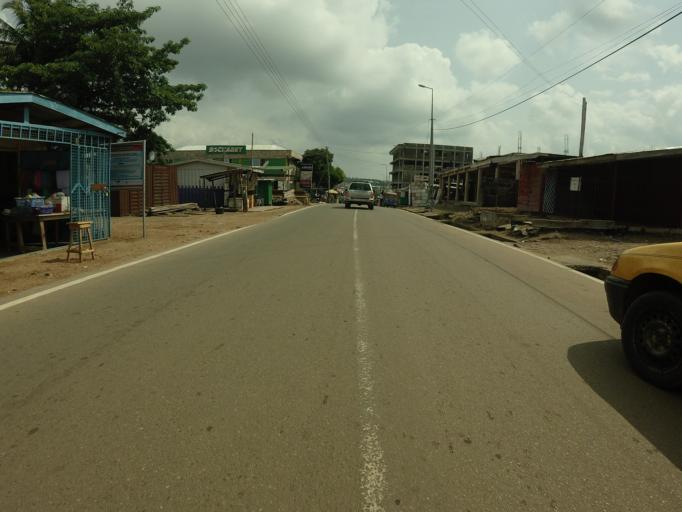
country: GH
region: Volta
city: Ho
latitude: 6.6183
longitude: 0.4737
